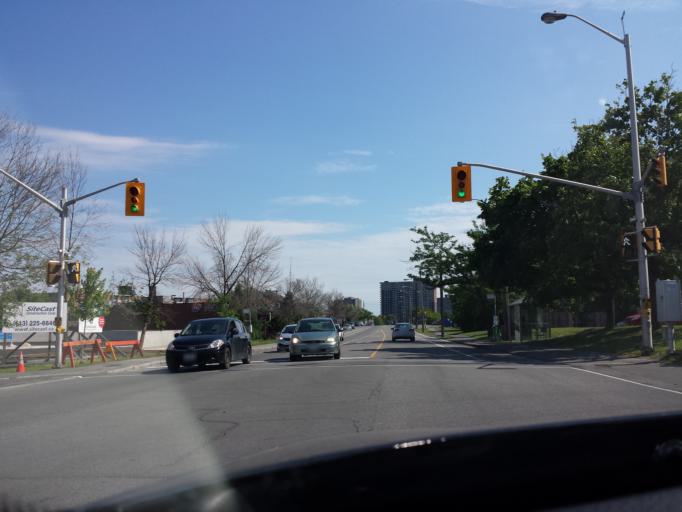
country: CA
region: Ontario
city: Bells Corners
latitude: 45.3628
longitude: -75.7902
